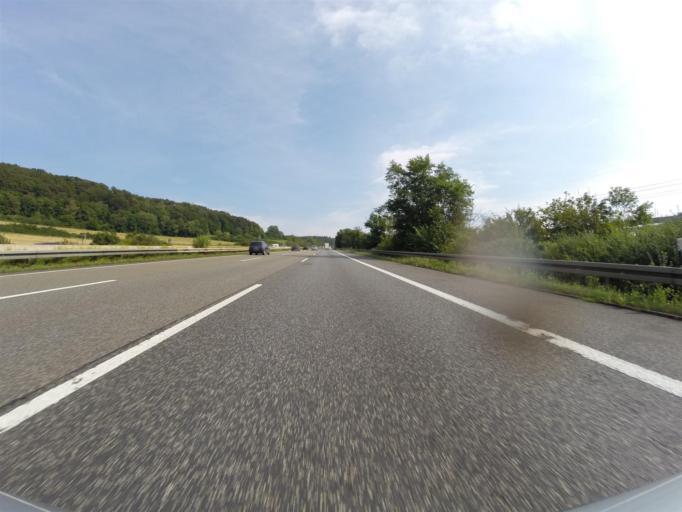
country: DE
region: Hesse
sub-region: Regierungsbezirk Kassel
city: Kirchheim
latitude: 50.8616
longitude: 9.5898
